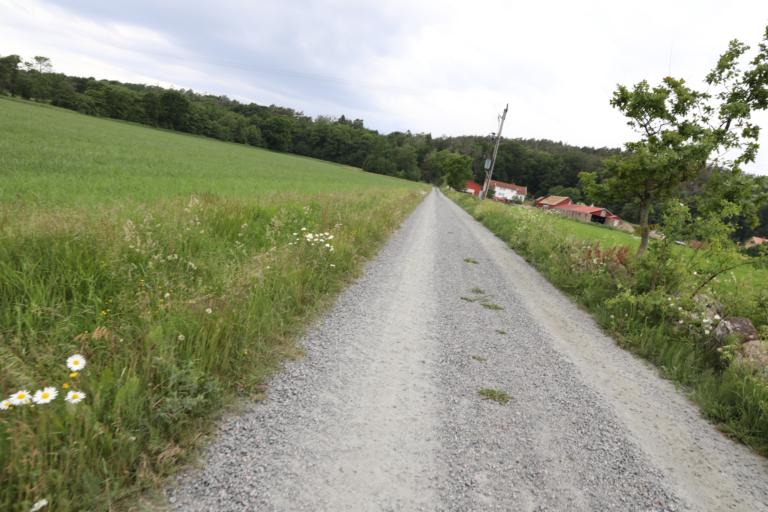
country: SE
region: Halland
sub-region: Varbergs Kommun
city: Varberg
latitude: 57.1616
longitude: 12.2696
